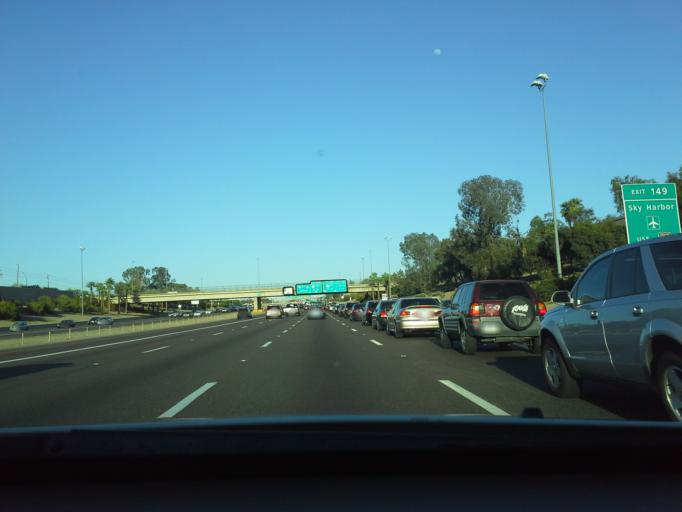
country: US
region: Arizona
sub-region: Maricopa County
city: Phoenix
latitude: 33.4617
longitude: -112.0592
